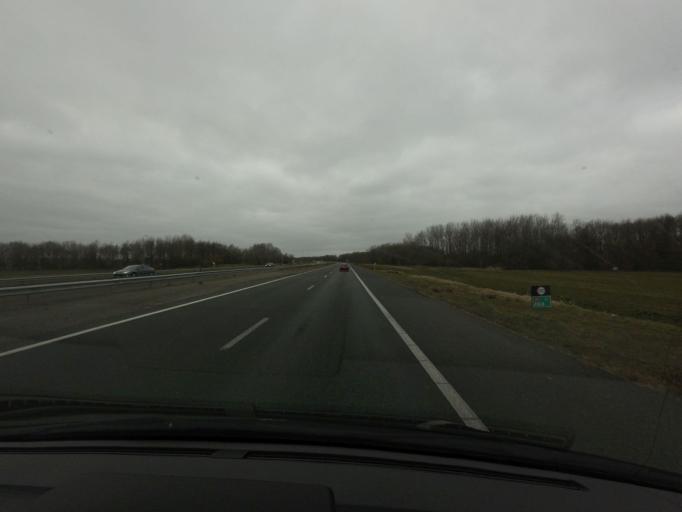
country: NL
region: Groningen
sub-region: Gemeente Hoogezand-Sappemeer
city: Hoogezand
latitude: 53.1952
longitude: 6.7007
